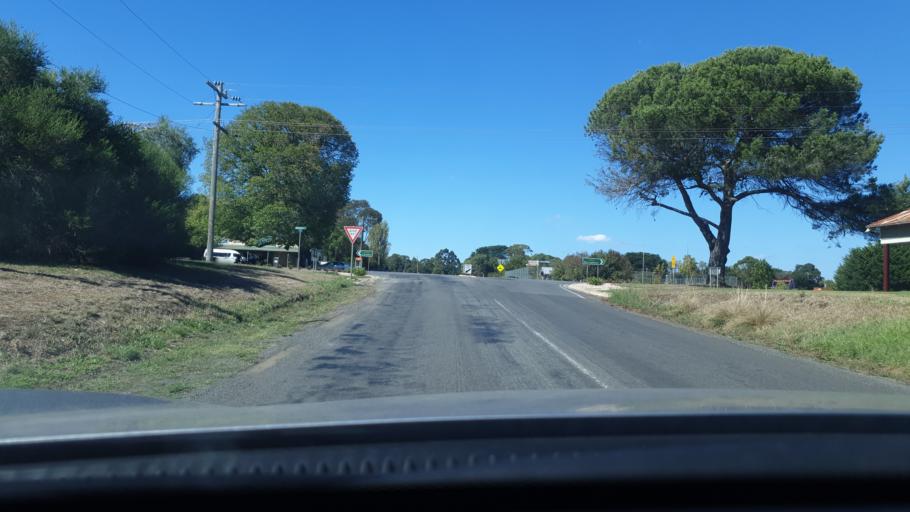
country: AU
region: Victoria
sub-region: Warrnambool
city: Warrnambool
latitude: -38.1845
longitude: 142.4310
